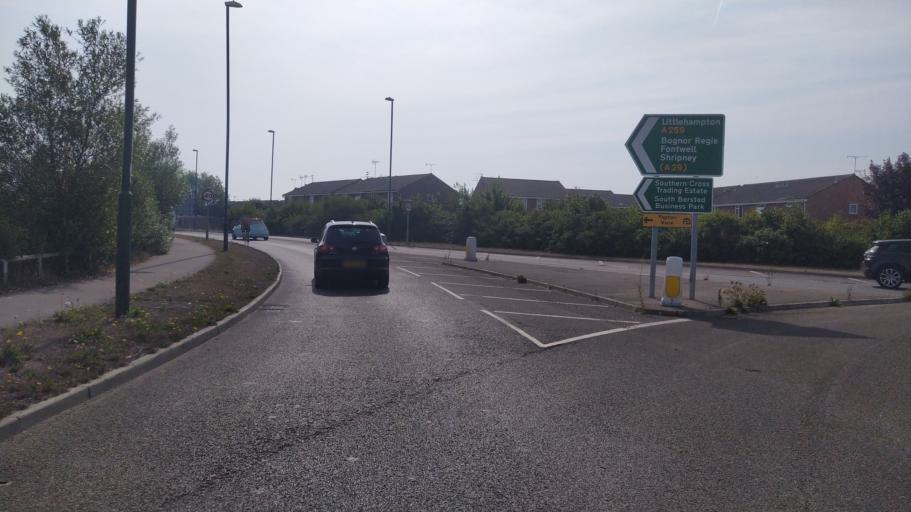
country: GB
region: England
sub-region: West Sussex
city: Bognor Regis
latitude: 50.8041
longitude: -0.6784
